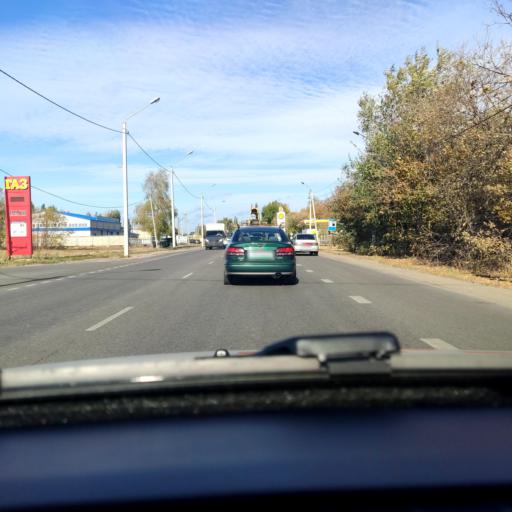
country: RU
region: Voronezj
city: Voronezh
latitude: 51.6158
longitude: 39.1784
